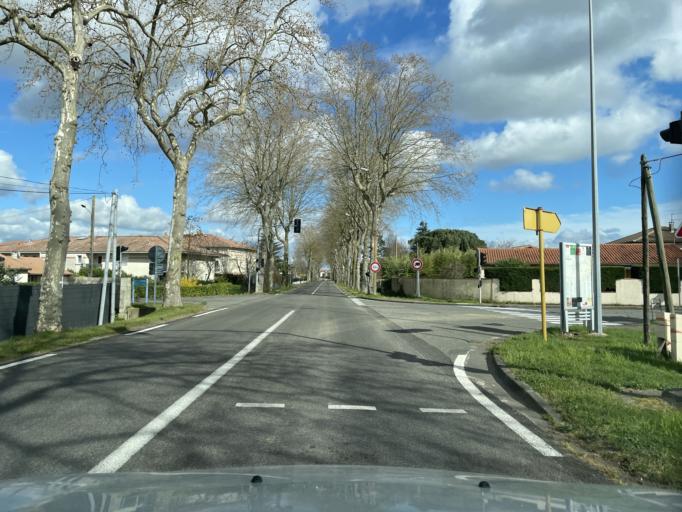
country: FR
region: Midi-Pyrenees
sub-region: Departement de la Haute-Garonne
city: Leguevin
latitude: 43.5986
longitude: 1.2256
